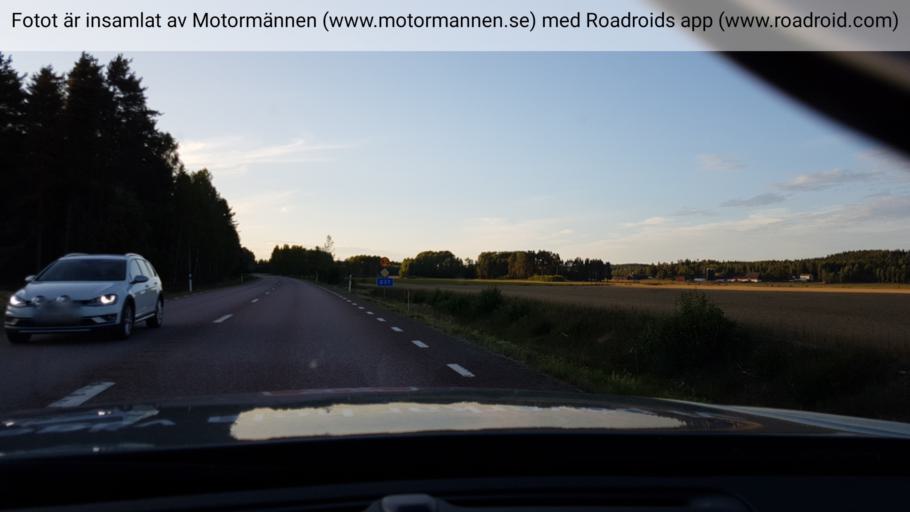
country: SE
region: OErebro
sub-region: Karlskoga Kommun
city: Karlskoga
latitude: 59.4046
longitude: 14.4312
